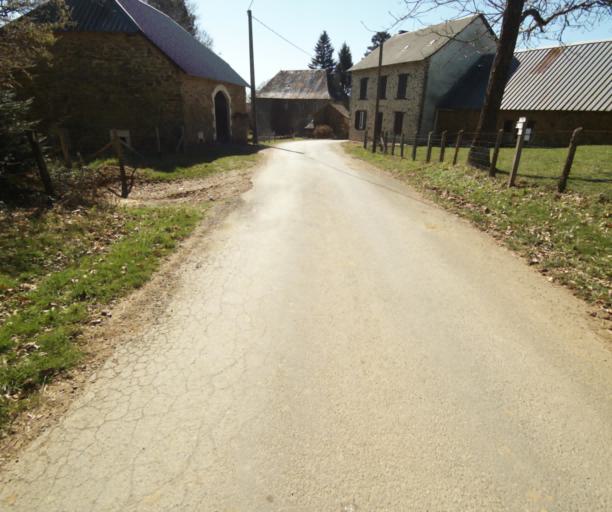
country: FR
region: Limousin
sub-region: Departement de la Correze
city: Seilhac
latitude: 45.3509
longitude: 1.7290
